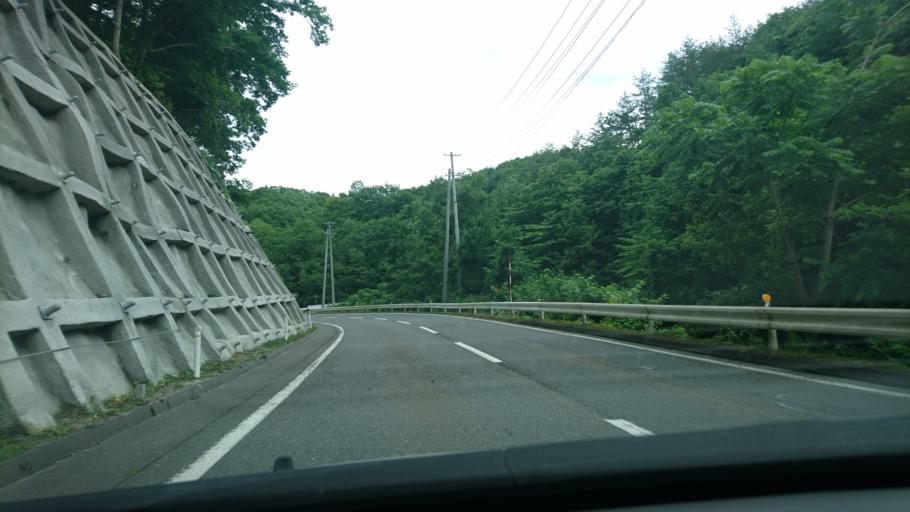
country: JP
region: Iwate
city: Miyako
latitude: 39.9673
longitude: 141.8580
